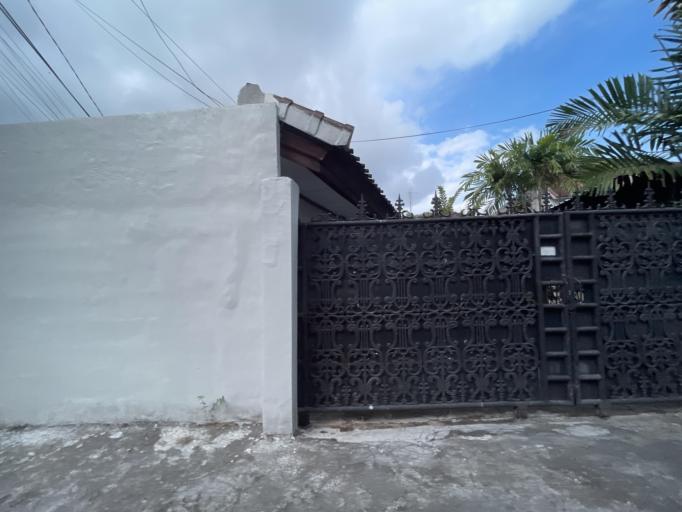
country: ID
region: Bali
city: Kuta
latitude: -8.6726
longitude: 115.1690
